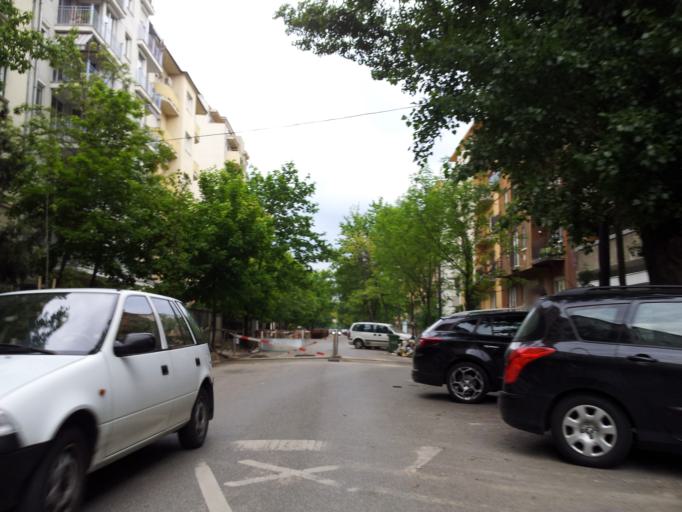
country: HU
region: Budapest
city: Budapest XI. keruelet
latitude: 47.4741
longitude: 19.0408
